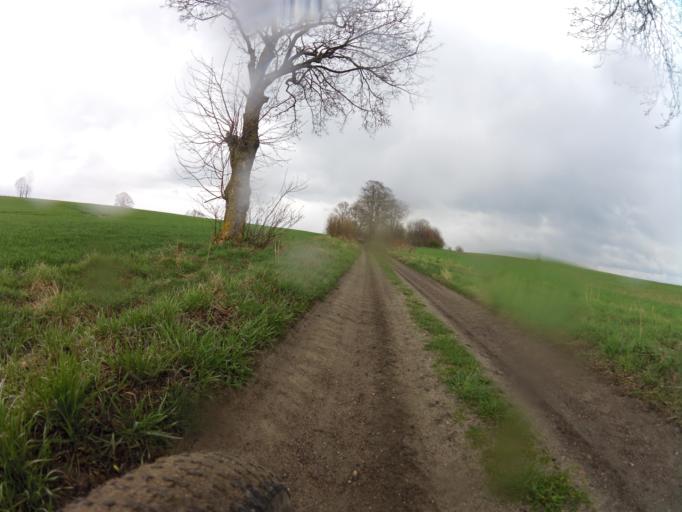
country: PL
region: West Pomeranian Voivodeship
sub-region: Powiat koszalinski
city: Polanow
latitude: 54.2152
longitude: 16.7594
